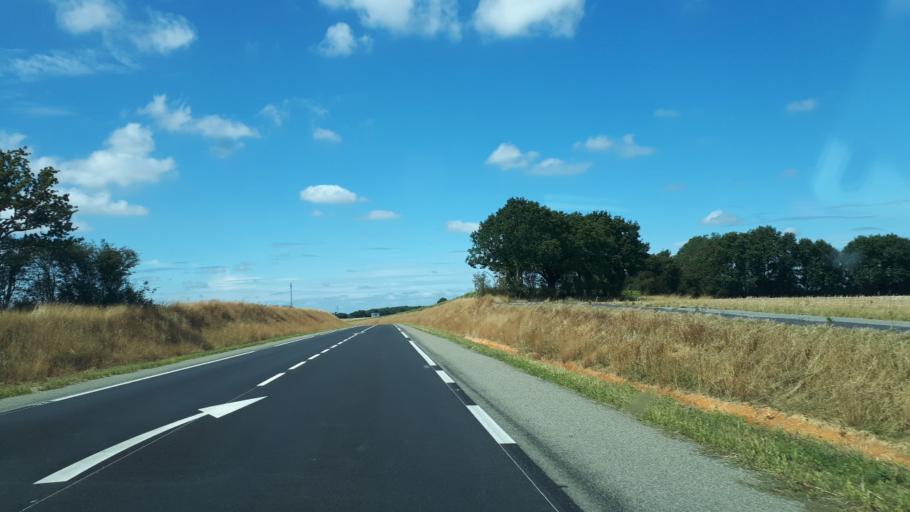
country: FR
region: Pays de la Loire
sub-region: Departement de la Sarthe
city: Saint-Calais
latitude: 47.9315
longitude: 0.7230
